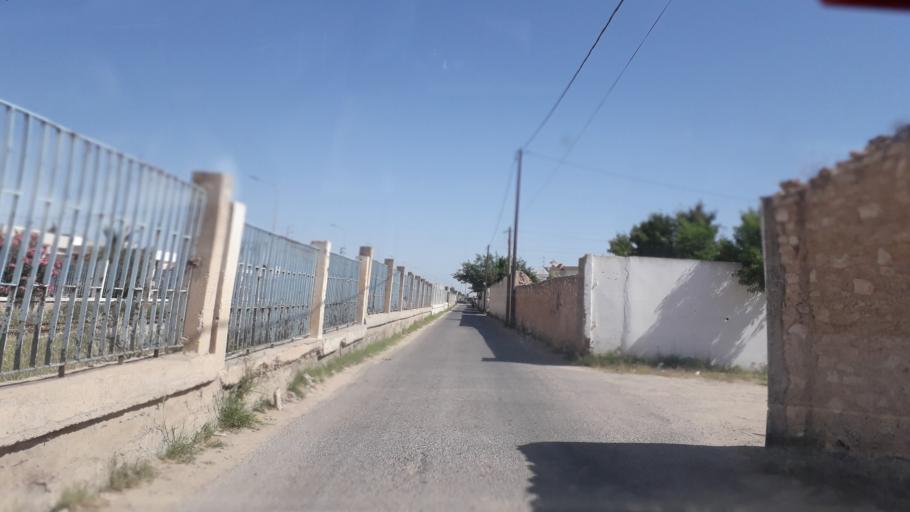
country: TN
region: Safaqis
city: Al Qarmadah
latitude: 34.8091
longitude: 10.7619
